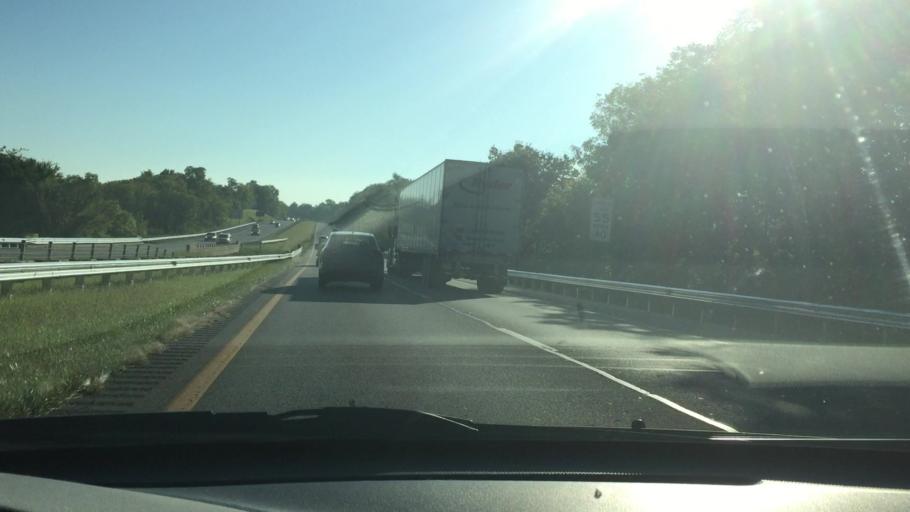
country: US
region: Kentucky
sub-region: Fayette County
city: Lexington
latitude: 37.9919
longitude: -84.4829
